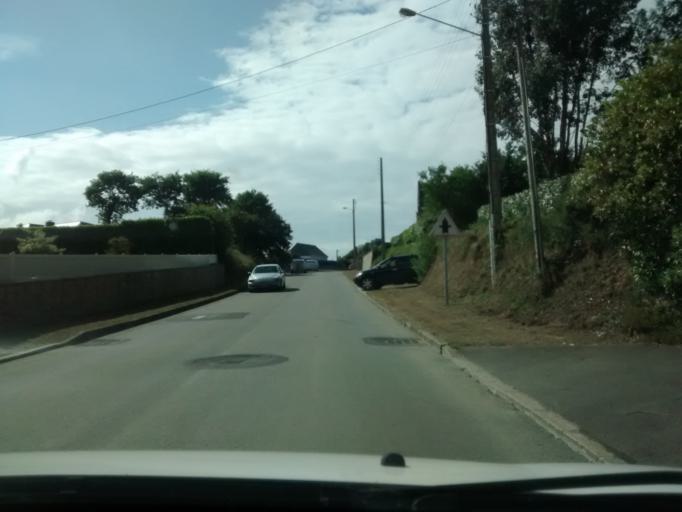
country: FR
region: Brittany
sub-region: Departement des Cotes-d'Armor
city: Penvenan
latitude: 48.8030
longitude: -3.2903
